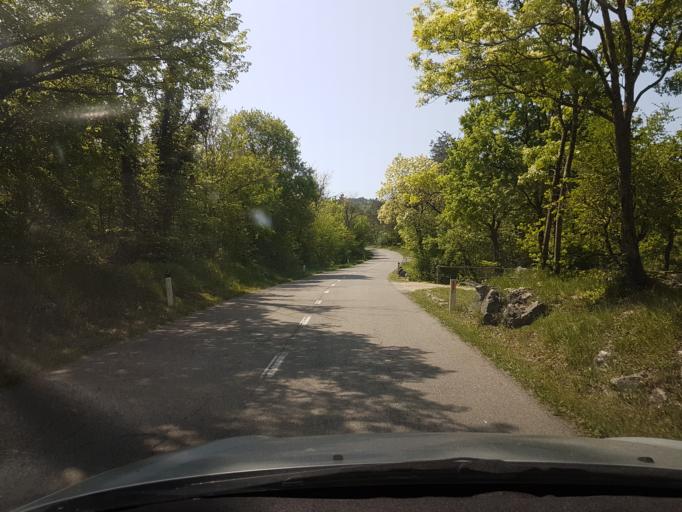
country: IT
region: Friuli Venezia Giulia
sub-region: Provincia di Trieste
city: Aurisina
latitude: 45.7849
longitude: 13.7009
